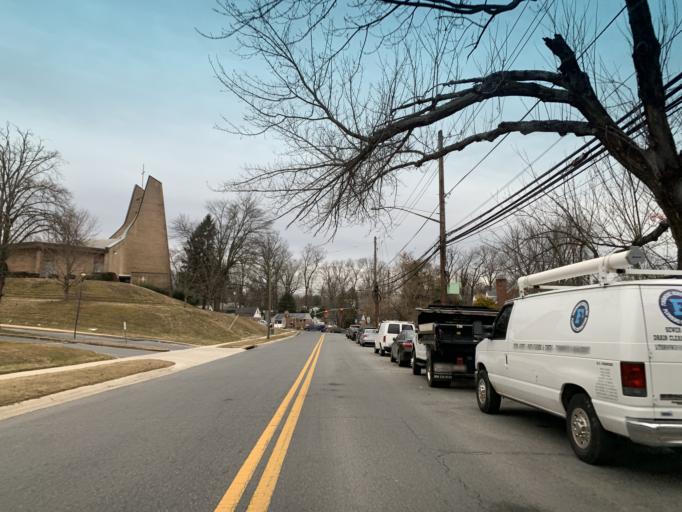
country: US
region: Maryland
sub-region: Montgomery County
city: Wheaton
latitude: 39.0495
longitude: -77.0683
